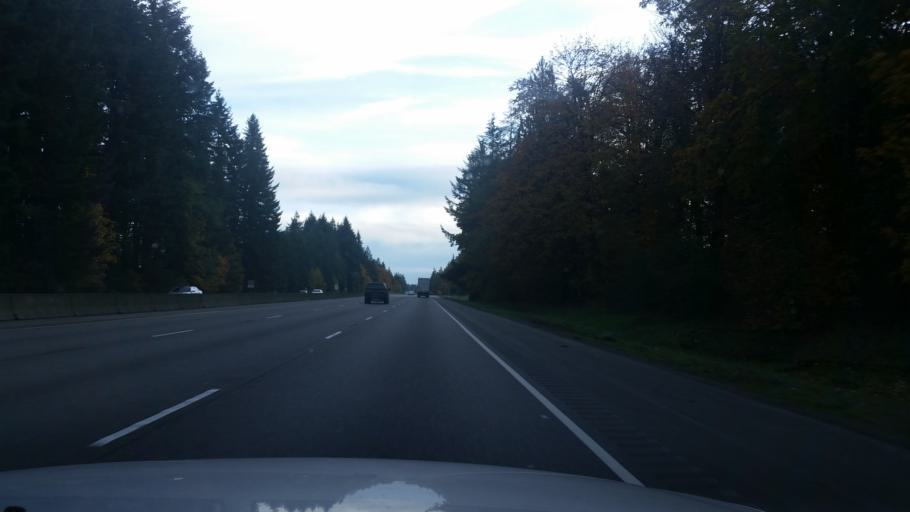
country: US
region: Washington
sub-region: Thurston County
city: Tumwater
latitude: 46.9522
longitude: -122.9378
